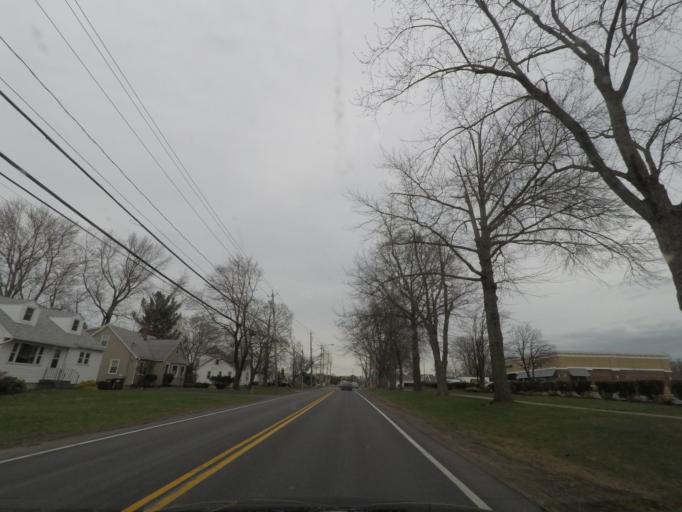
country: US
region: New York
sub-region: Albany County
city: Delmar
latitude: 42.6017
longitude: -73.7949
